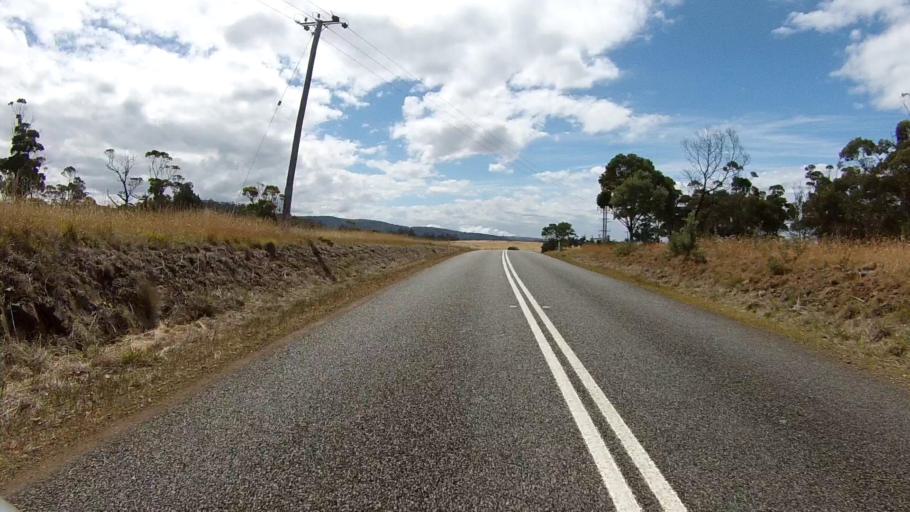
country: AU
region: Tasmania
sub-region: Sorell
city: Sorell
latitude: -42.2836
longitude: 147.9980
